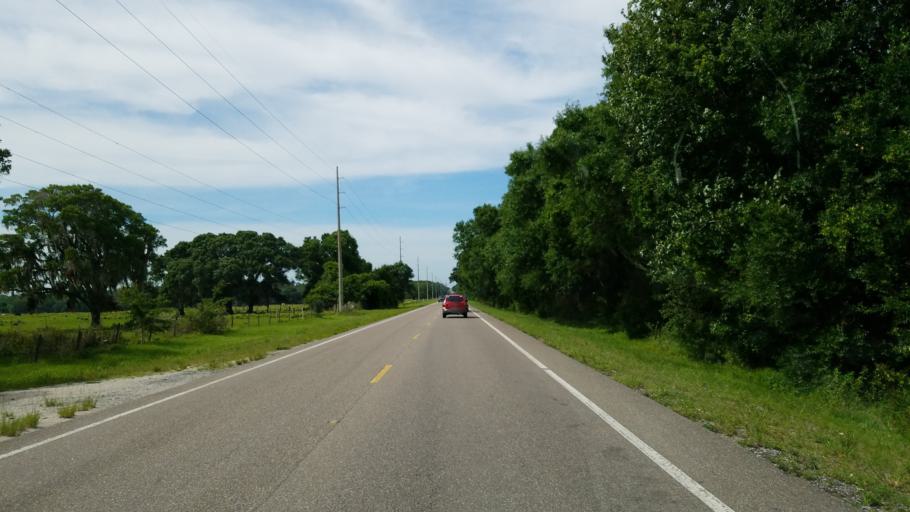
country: US
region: Florida
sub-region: Hillsborough County
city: Balm
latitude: 27.6794
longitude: -82.1462
